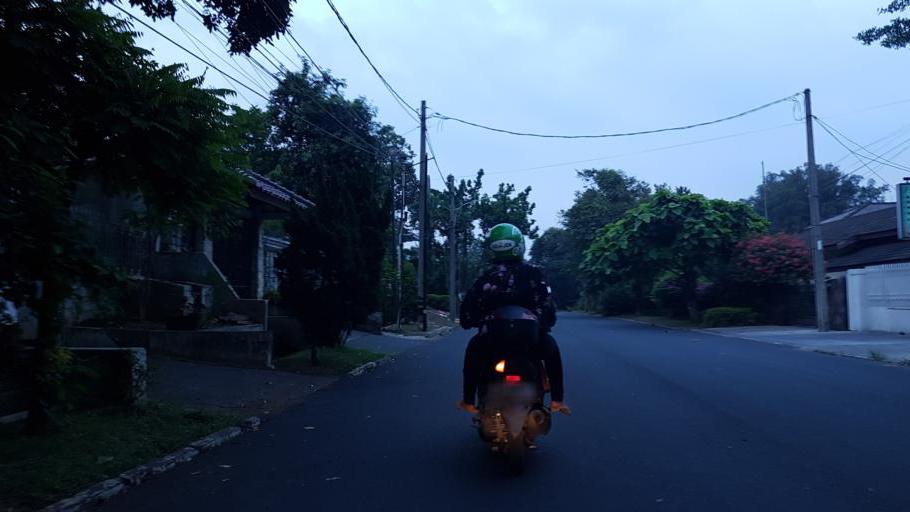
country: ID
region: West Java
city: Pamulang
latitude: -6.3154
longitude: 106.7848
